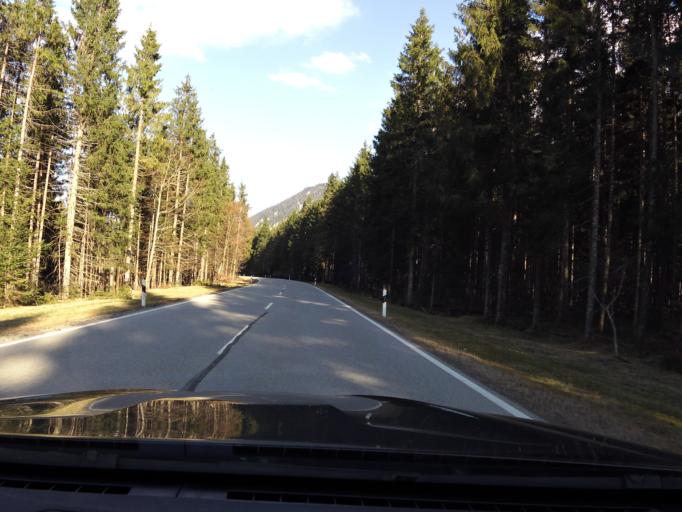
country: DE
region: Bavaria
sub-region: Upper Bavaria
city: Jachenau
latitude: 47.5567
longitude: 11.4466
